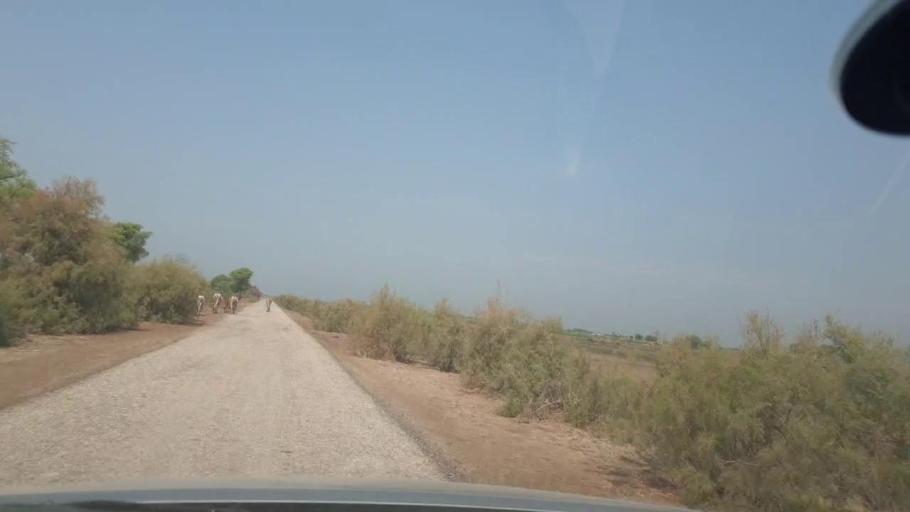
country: PK
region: Balochistan
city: Mehrabpur
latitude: 28.0608
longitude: 68.0695
